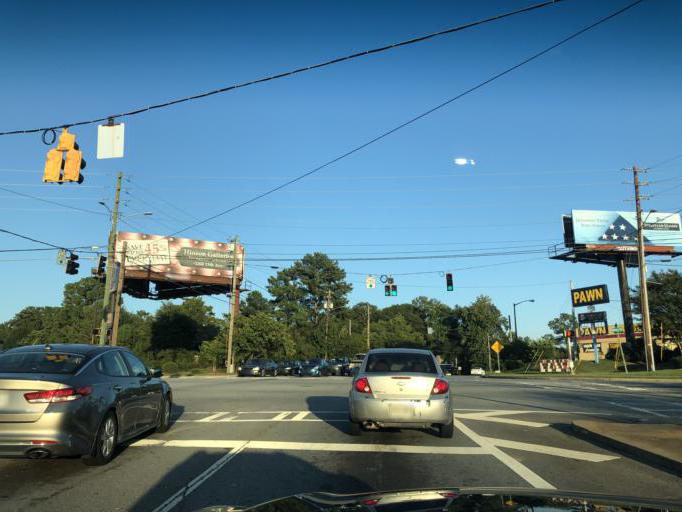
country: US
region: Georgia
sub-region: Muscogee County
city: Columbus
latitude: 32.5223
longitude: -84.8887
